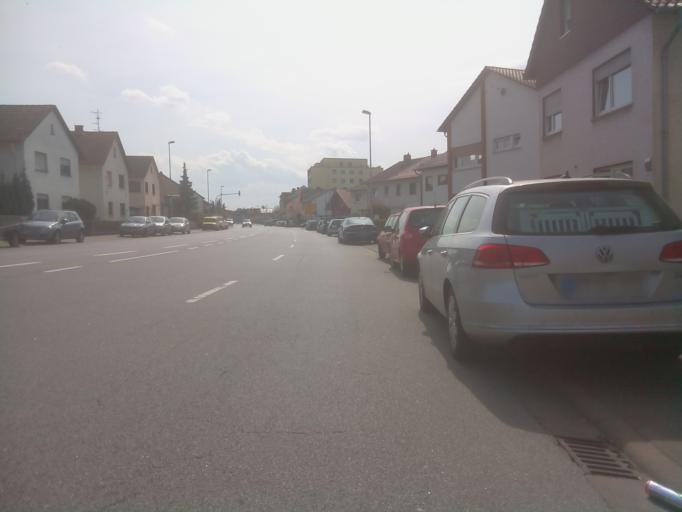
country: DE
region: Hesse
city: Lampertheim
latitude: 49.6043
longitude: 8.4616
